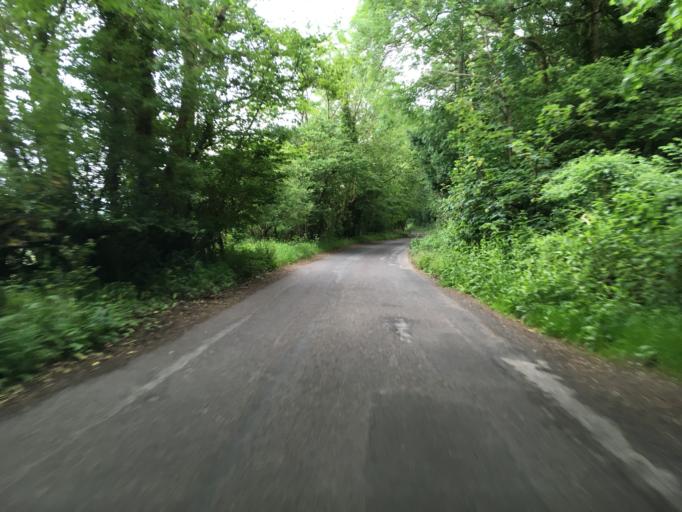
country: GB
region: England
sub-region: North Somerset
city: Clevedon
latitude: 51.4465
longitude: -2.8241
